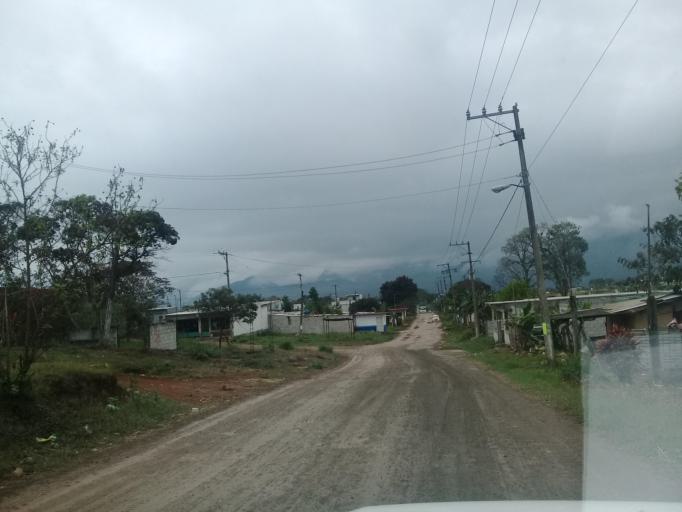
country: MX
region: Veracruz
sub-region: Cordoba
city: San Jose de Tapia
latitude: 18.8462
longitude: -96.9676
